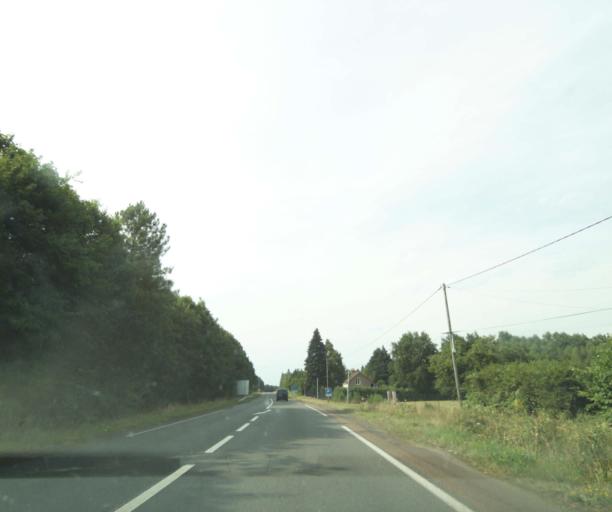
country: FR
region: Pays de la Loire
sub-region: Departement de la Sarthe
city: Marigne-Laille
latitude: 47.7763
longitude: 0.3444
